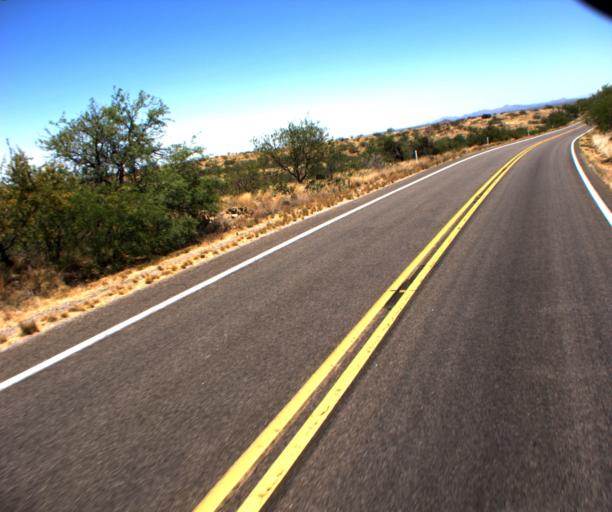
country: US
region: Arizona
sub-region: Pima County
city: Catalina
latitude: 32.6079
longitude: -110.9863
